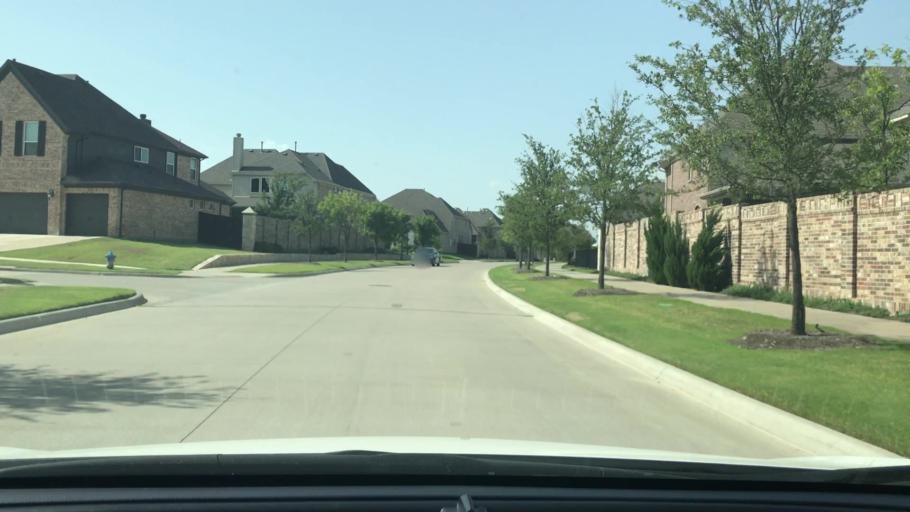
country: US
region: Texas
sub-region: Collin County
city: Frisco
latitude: 33.1326
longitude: -96.7649
